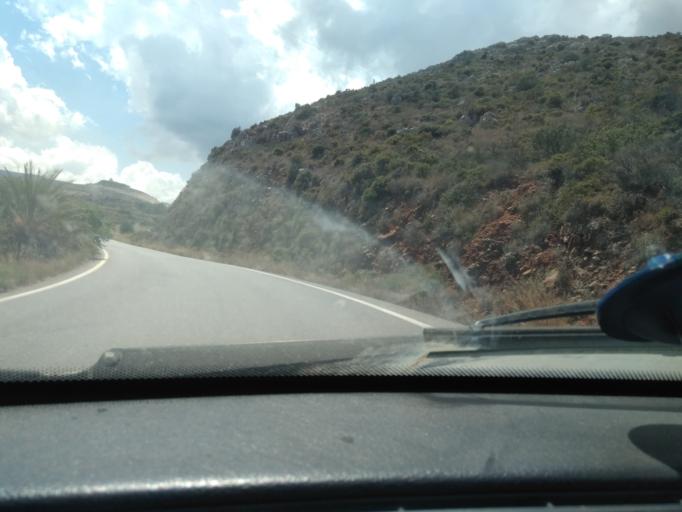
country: GR
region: Crete
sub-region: Nomos Lasithiou
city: Siteia
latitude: 35.1131
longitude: 26.0564
